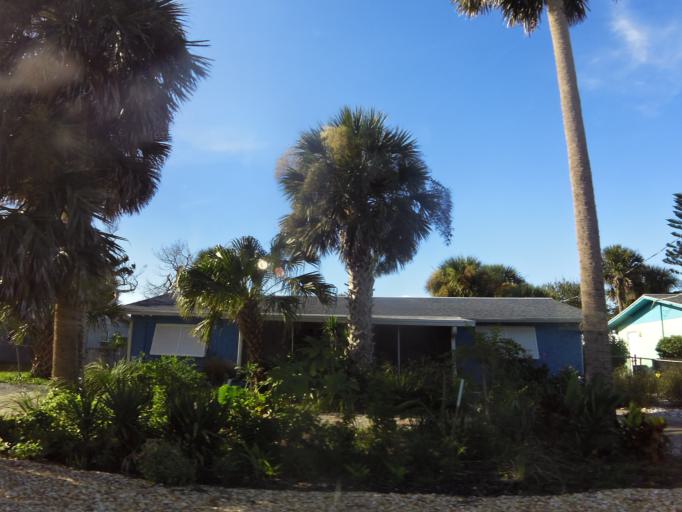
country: US
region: Florida
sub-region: Flagler County
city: Flagler Beach
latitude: 29.4826
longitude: -81.1314
